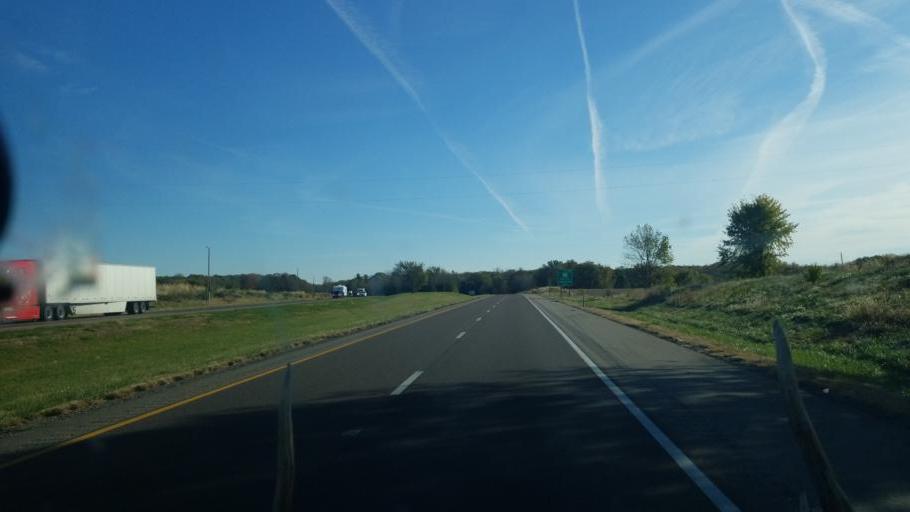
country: US
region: Illinois
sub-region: Madison County
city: Saint Jacob
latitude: 38.7657
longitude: -89.7641
